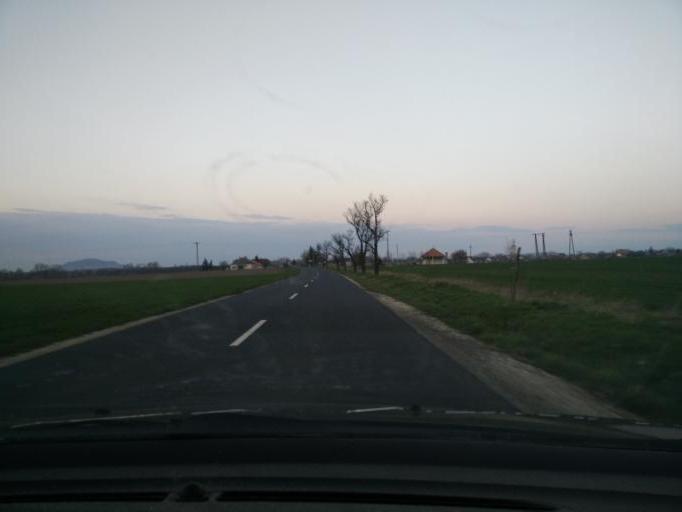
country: HU
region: Veszprem
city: Csabrendek
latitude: 47.0404
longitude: 17.3192
